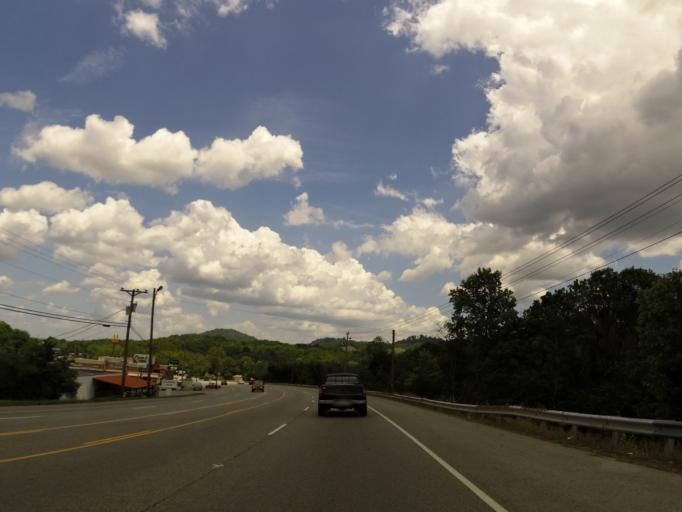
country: US
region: Tennessee
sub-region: Claiborne County
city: Tazewell
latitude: 36.4479
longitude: -83.5732
